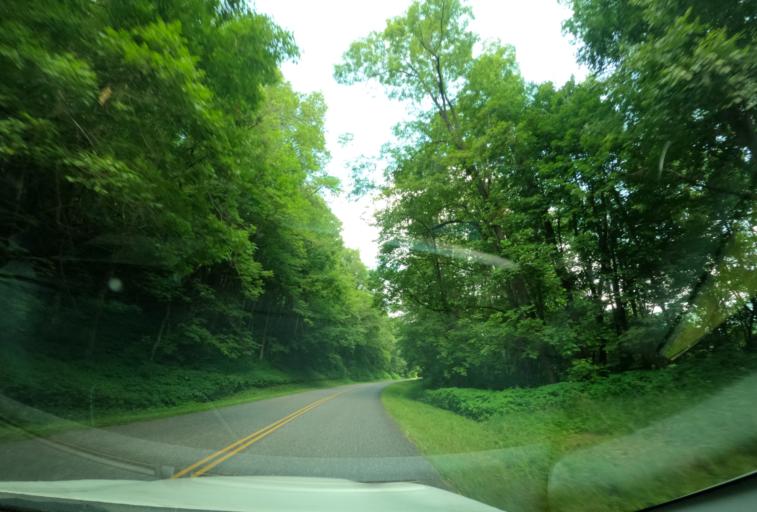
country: US
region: North Carolina
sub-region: Haywood County
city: Hazelwood
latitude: 35.4369
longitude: -83.0565
